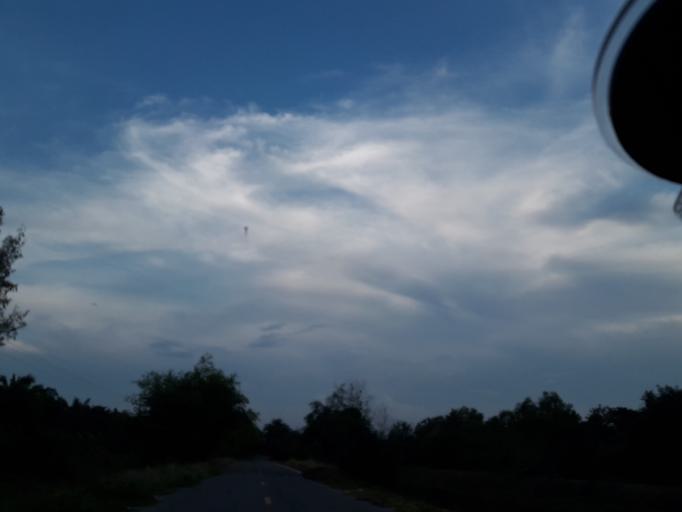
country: TH
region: Pathum Thani
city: Nong Suea
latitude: 14.2318
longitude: 100.8689
